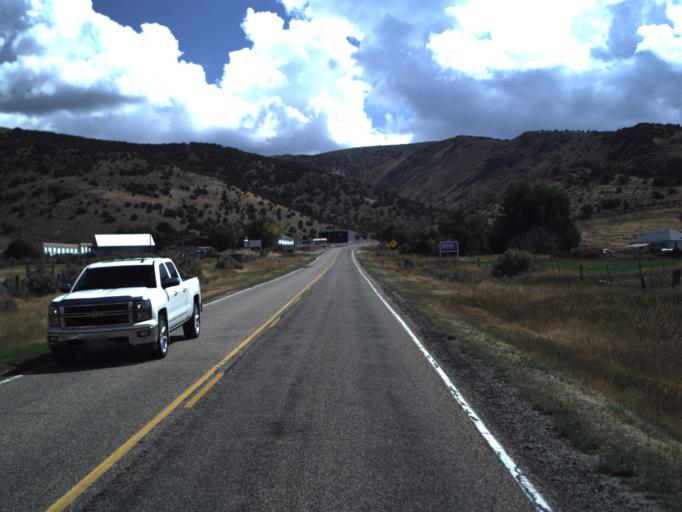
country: US
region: Utah
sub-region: Rich County
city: Randolph
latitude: 41.8291
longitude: -111.3168
